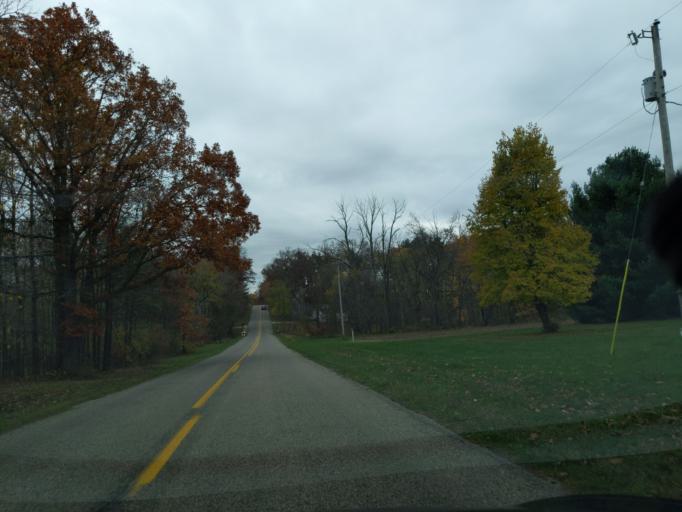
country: US
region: Michigan
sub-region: Eaton County
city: Eaton Rapids
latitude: 42.4993
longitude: -84.6012
